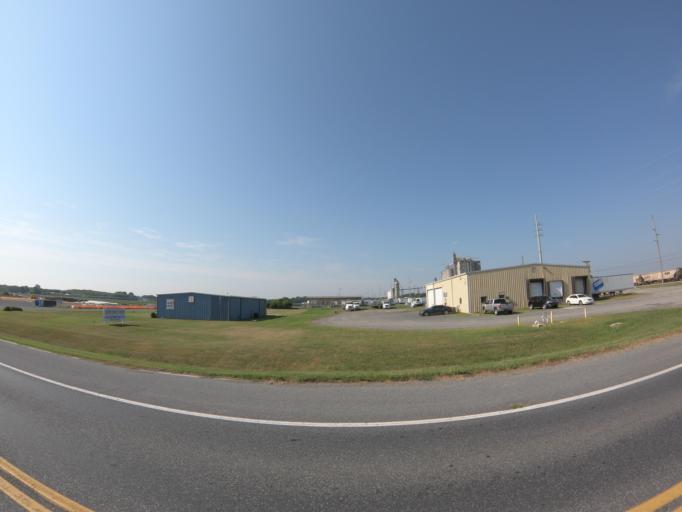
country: US
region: Delaware
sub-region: Sussex County
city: Bridgeville
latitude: 38.7612
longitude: -75.6010
